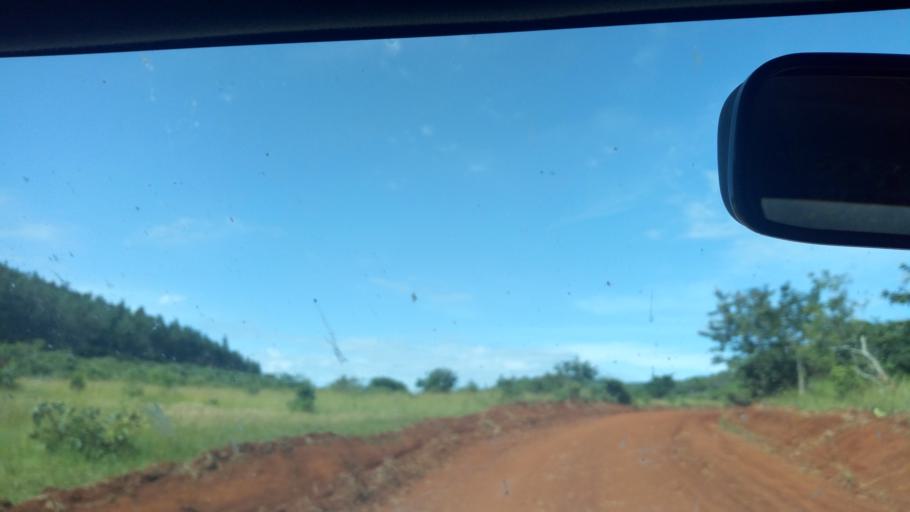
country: UG
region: Western Region
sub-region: Masindi District
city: Masindi
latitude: 1.6463
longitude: 31.7755
